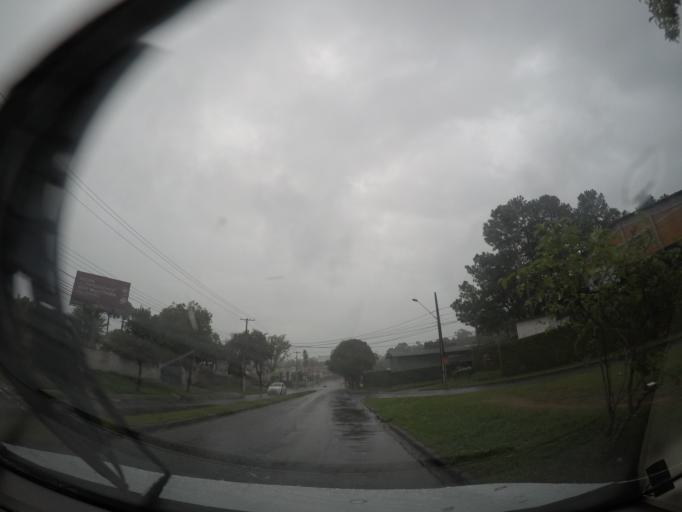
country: BR
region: Parana
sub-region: Curitiba
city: Curitiba
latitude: -25.4508
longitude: -49.3558
